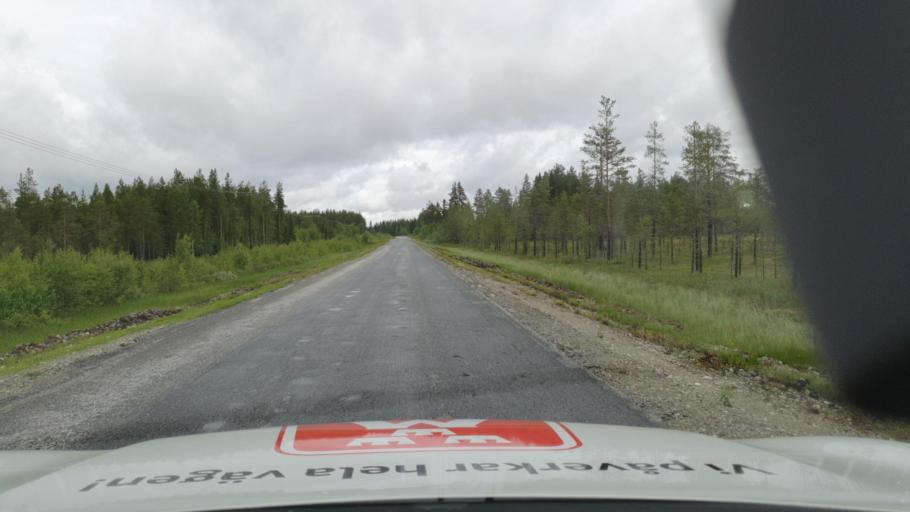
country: SE
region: Vaesterbotten
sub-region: Dorotea Kommun
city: Dorotea
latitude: 64.1339
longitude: 16.6377
